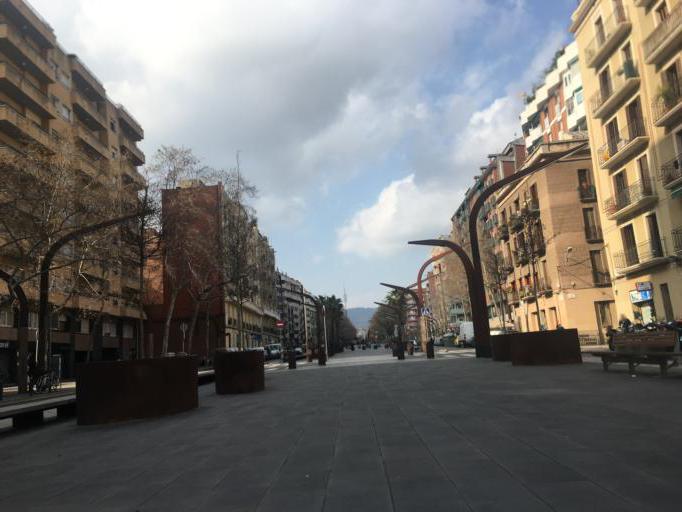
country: ES
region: Catalonia
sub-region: Provincia de Barcelona
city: les Corts
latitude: 41.3743
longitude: 2.1308
